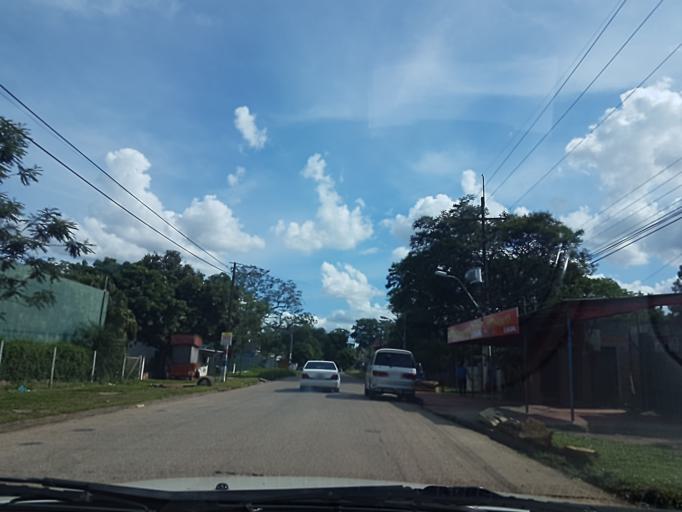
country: PY
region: Central
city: Colonia Mariano Roque Alonso
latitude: -25.1953
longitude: -57.5348
